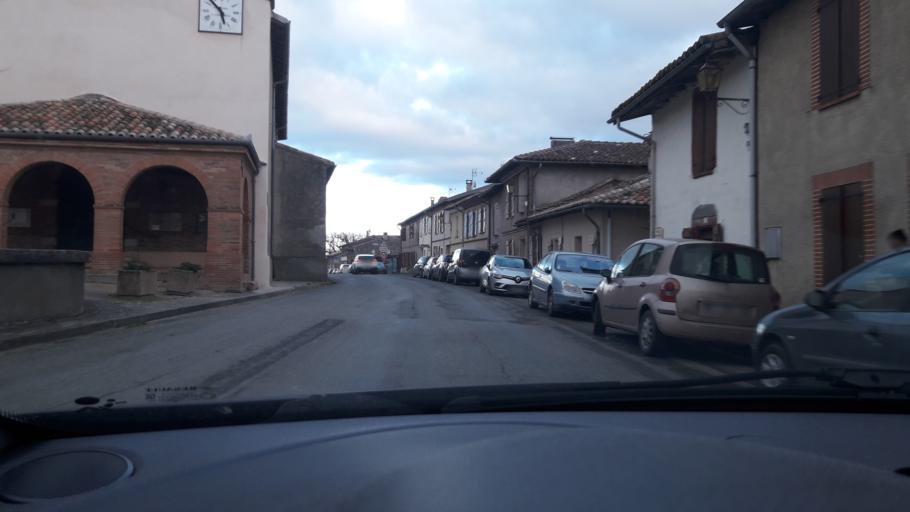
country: FR
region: Midi-Pyrenees
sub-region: Departement de la Haute-Garonne
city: Launac
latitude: 43.7384
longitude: 1.1169
